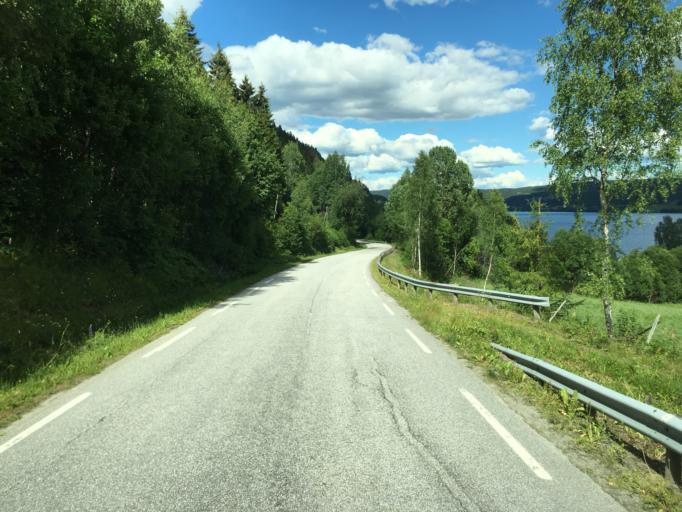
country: NO
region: Oppland
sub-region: Sondre Land
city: Hov
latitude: 60.5751
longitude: 10.2890
